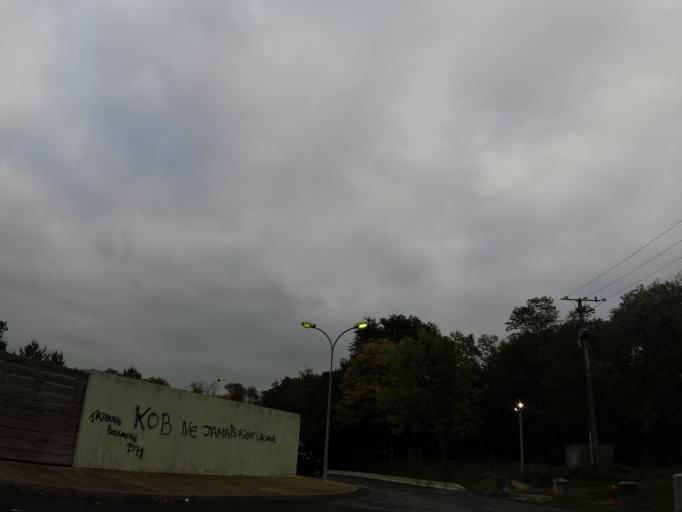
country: FR
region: Ile-de-France
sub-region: Departement de Seine-et-Marne
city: Sammeron
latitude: 48.9702
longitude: 3.0645
